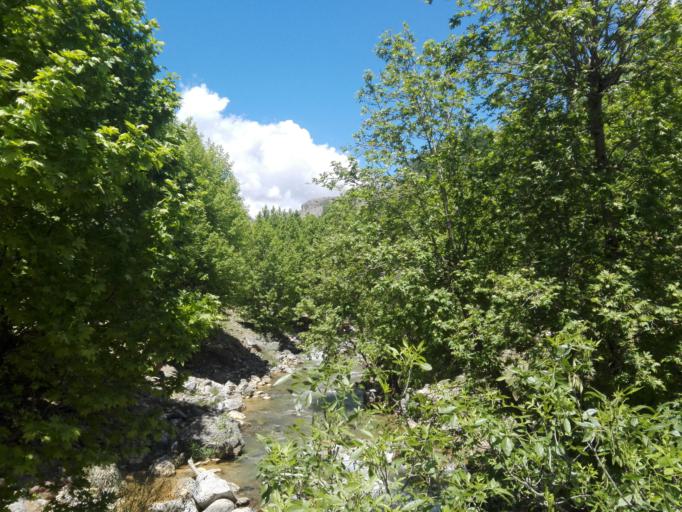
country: TR
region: Batman
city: Kozluk
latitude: 38.2198
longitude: 41.4813
